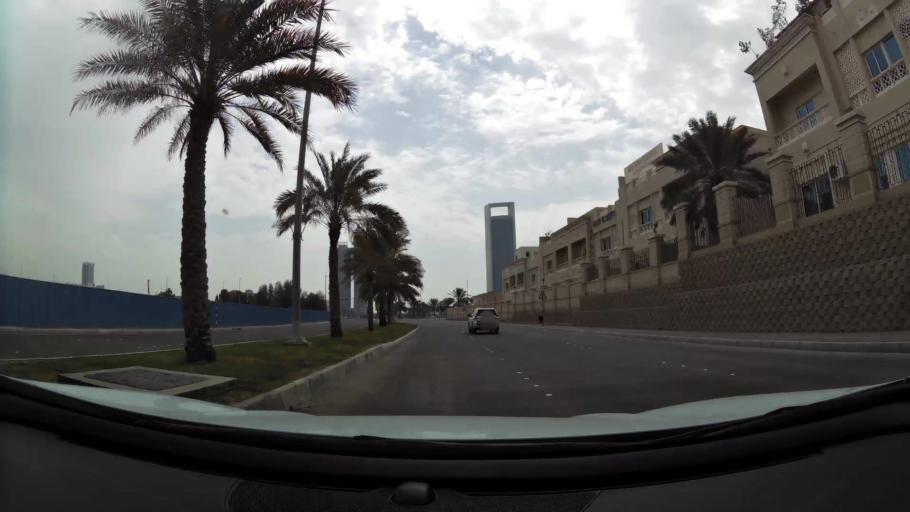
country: AE
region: Abu Dhabi
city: Abu Dhabi
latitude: 24.4733
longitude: 54.3194
